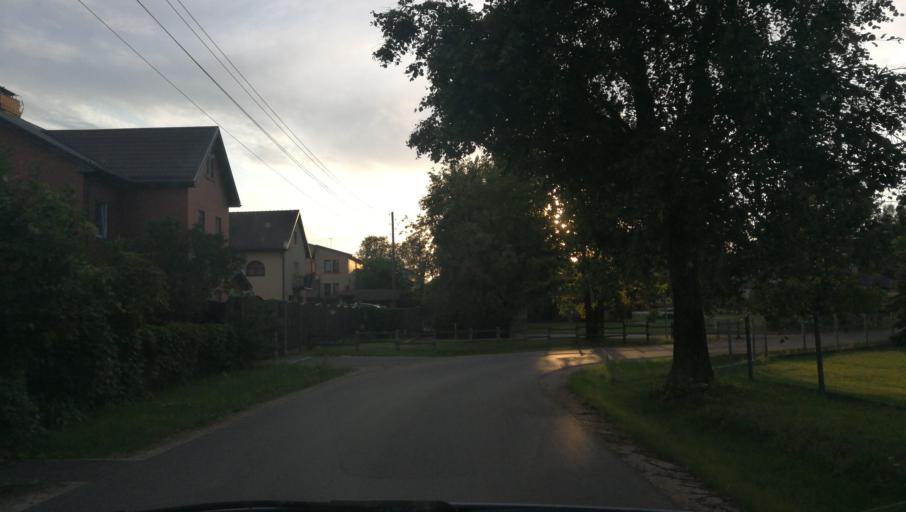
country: LV
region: Ikskile
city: Ikskile
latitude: 56.8368
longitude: 24.5130
